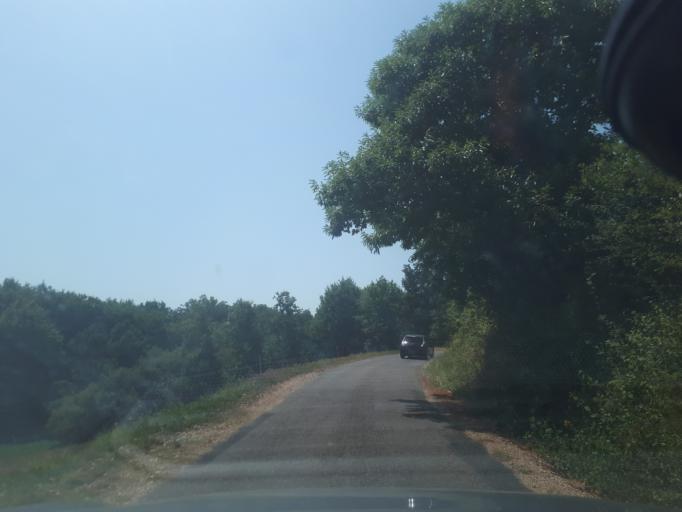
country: FR
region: Midi-Pyrenees
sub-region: Departement du Lot
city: Gourdon
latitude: 44.7415
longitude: 1.3279
